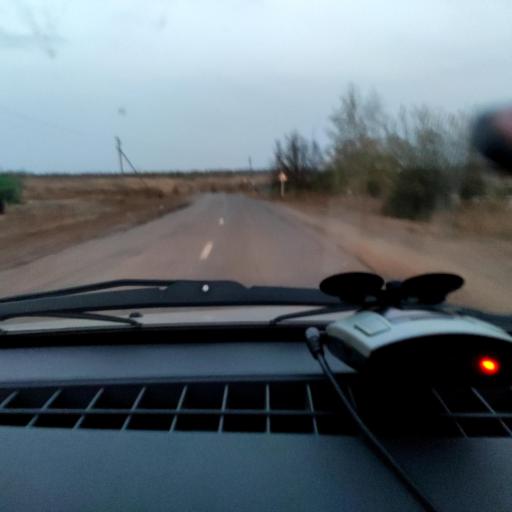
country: RU
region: Voronezj
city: Kolodeznyy
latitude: 51.2382
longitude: 39.0415
